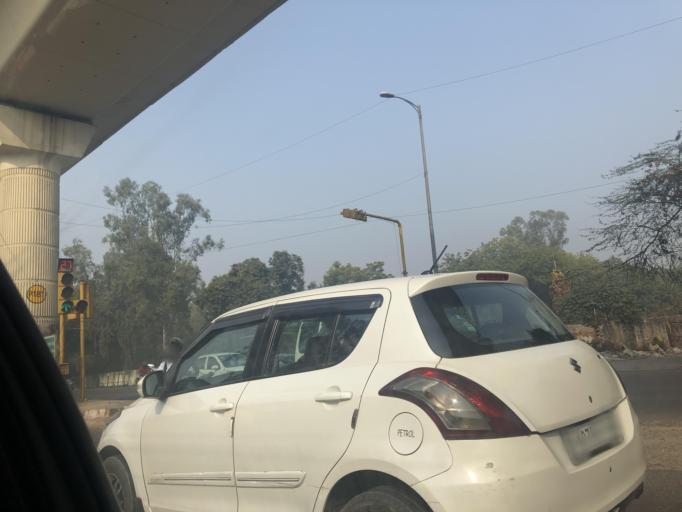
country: IN
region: NCT
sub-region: North West Delhi
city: Pitampura
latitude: 28.6762
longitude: 77.1193
